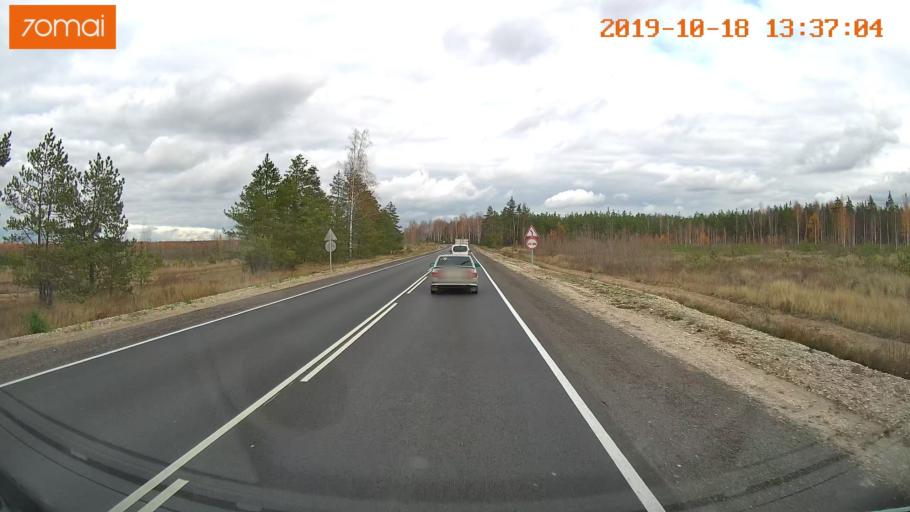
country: RU
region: Rjazan
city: Solotcha
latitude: 54.8762
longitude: 39.9911
